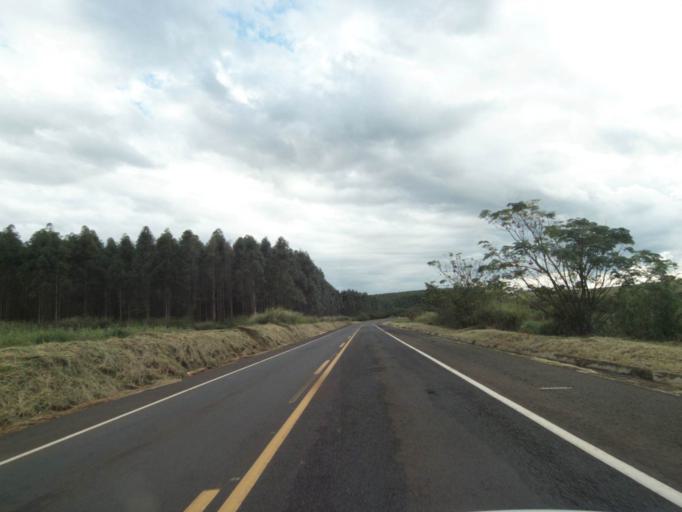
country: PY
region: Canindeyu
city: Salto del Guaira
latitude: -24.0849
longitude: -54.0785
